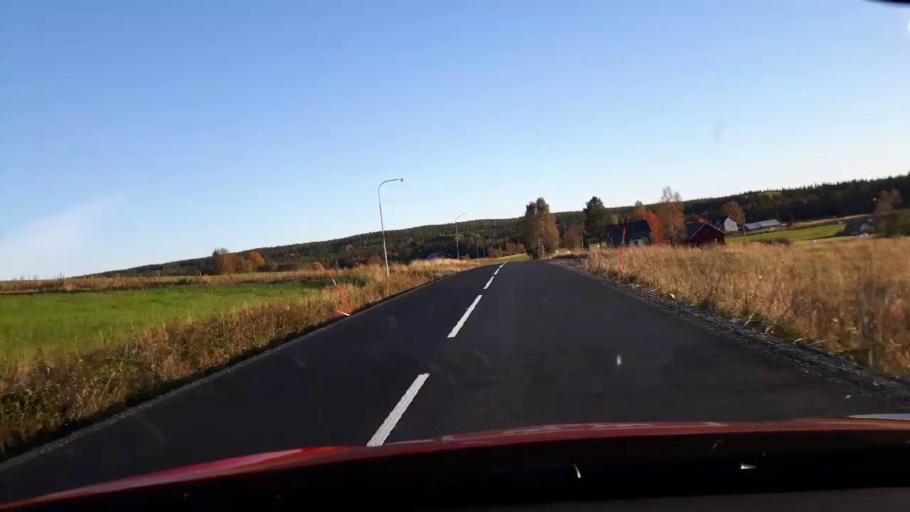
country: SE
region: Jaemtland
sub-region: OEstersunds Kommun
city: Lit
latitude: 63.4395
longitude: 14.8370
